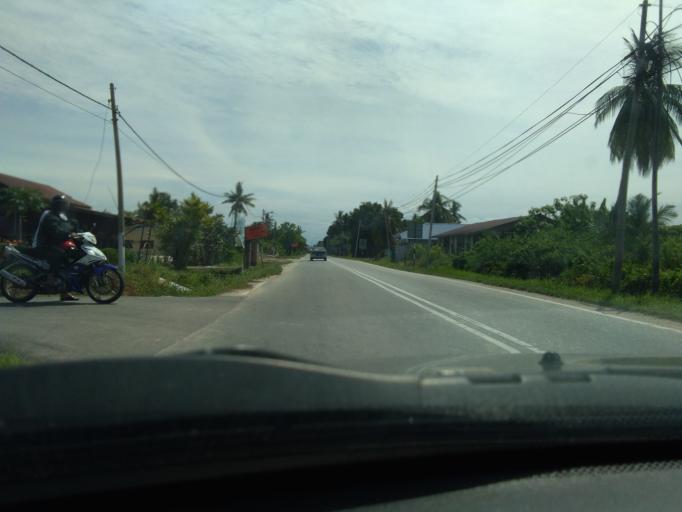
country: MY
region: Perak
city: Bagan Serai
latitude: 5.0146
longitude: 100.5395
